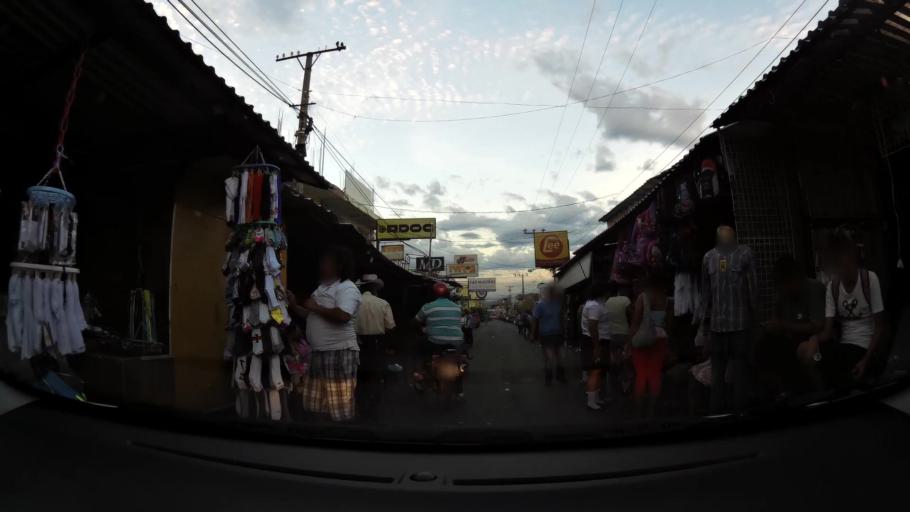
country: SV
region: San Vicente
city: San Vicente
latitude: 13.6444
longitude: -88.7866
